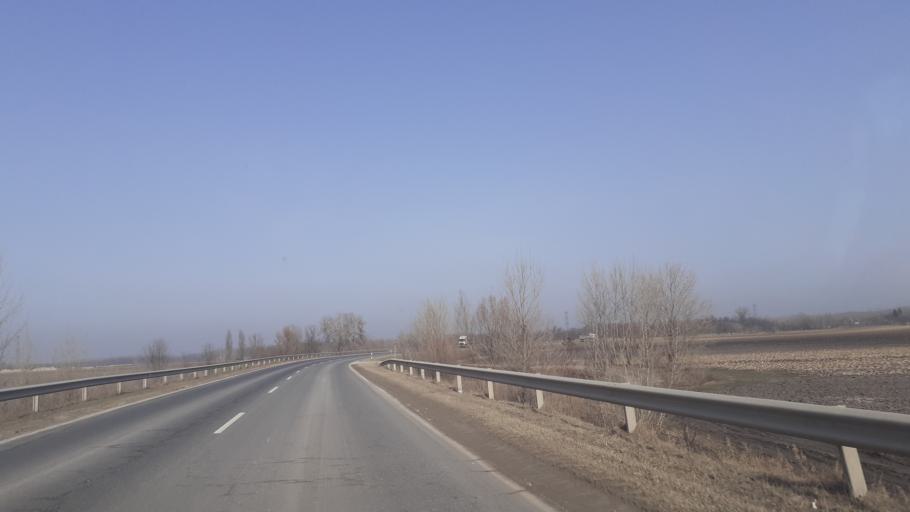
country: HU
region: Pest
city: Bugyi
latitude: 47.2384
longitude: 19.1210
